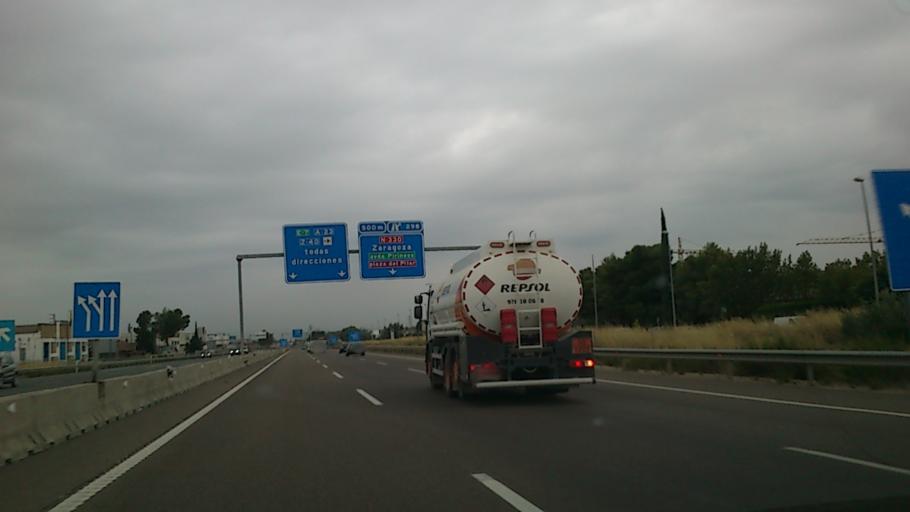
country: ES
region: Aragon
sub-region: Provincia de Zaragoza
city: Villanueva de Gallego
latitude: 41.7410
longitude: -0.8445
